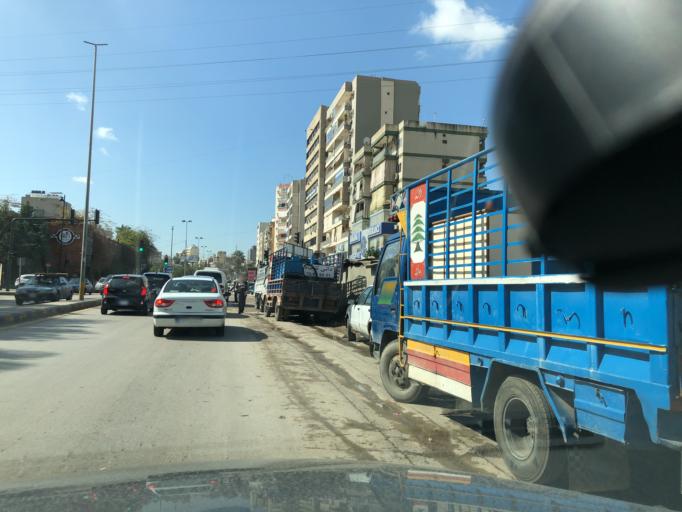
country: LB
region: Mont-Liban
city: Jdaidet el Matn
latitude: 33.8812
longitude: 35.5535
